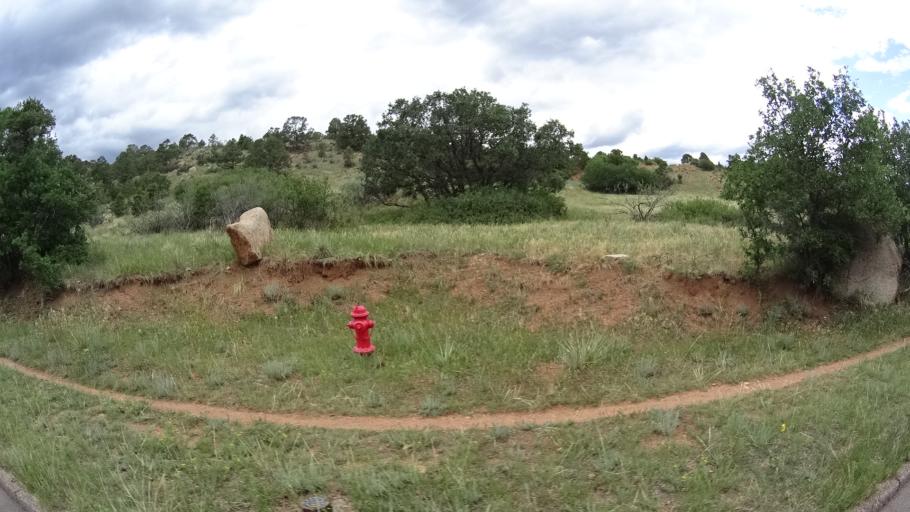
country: US
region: Colorado
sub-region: El Paso County
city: Manitou Springs
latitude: 38.8463
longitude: -104.8986
